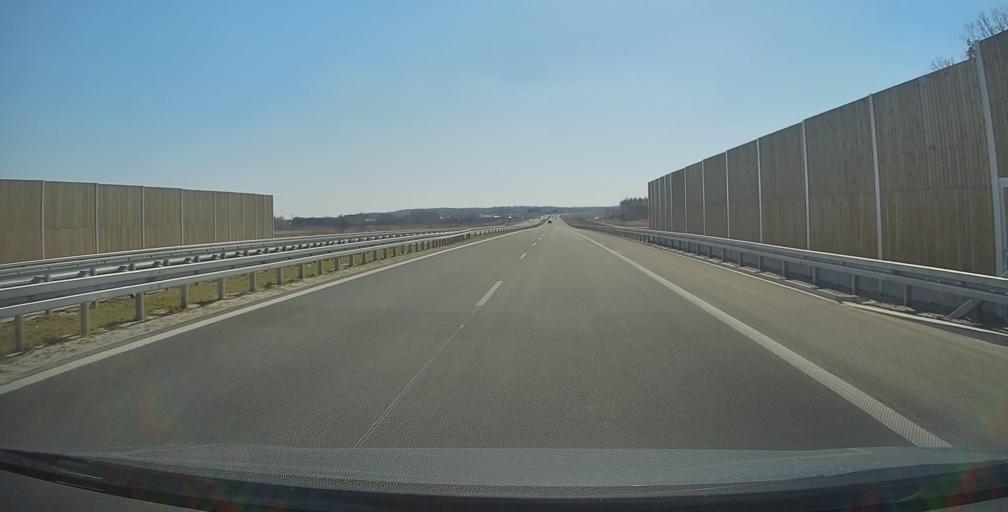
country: PL
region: Subcarpathian Voivodeship
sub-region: Powiat lezajski
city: Letownia
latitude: 50.3571
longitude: 22.1964
